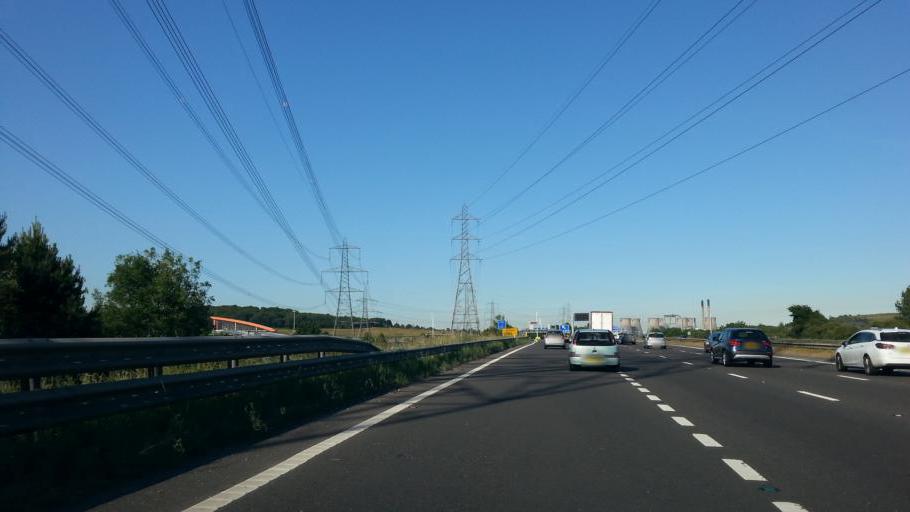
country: GB
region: England
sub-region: City and Borough of Wakefield
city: Pontefract
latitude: 53.7066
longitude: -1.3383
